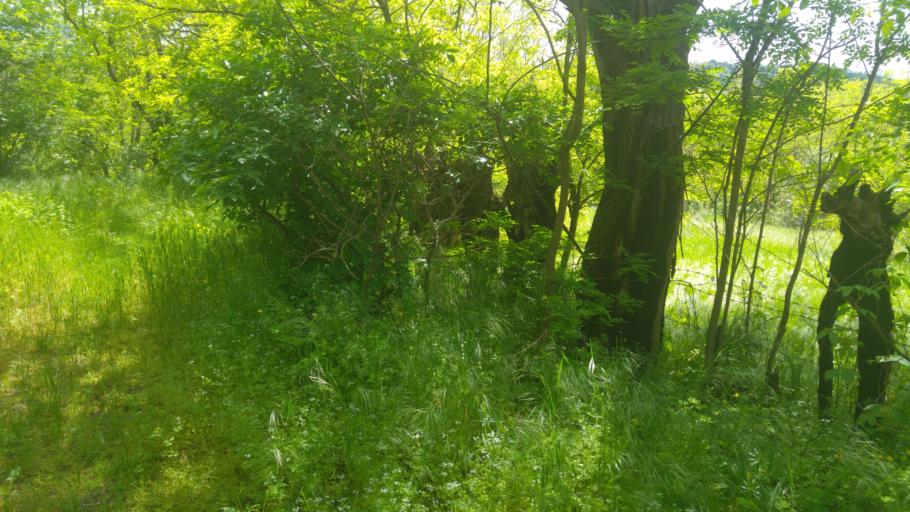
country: HU
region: Komarom-Esztergom
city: Kesztolc
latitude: 47.7141
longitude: 18.7933
